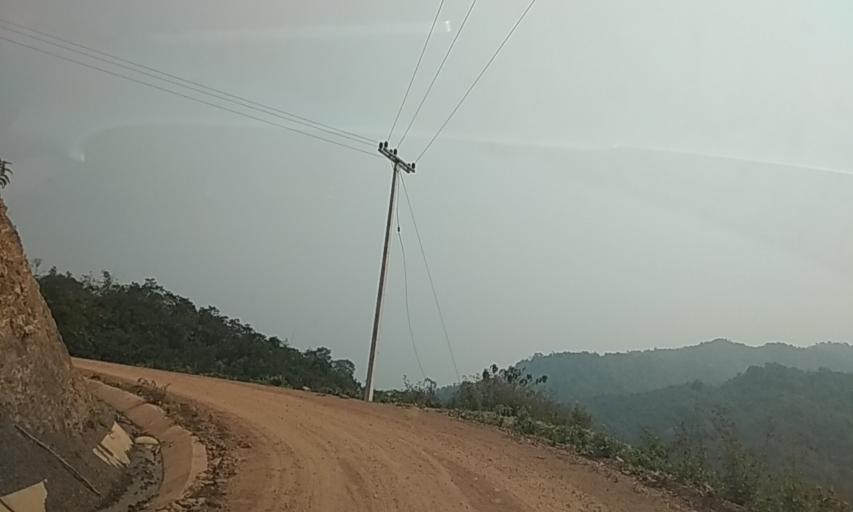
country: VN
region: Huyen Dien Bien
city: Dien Bien Phu
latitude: 21.4381
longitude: 102.7677
